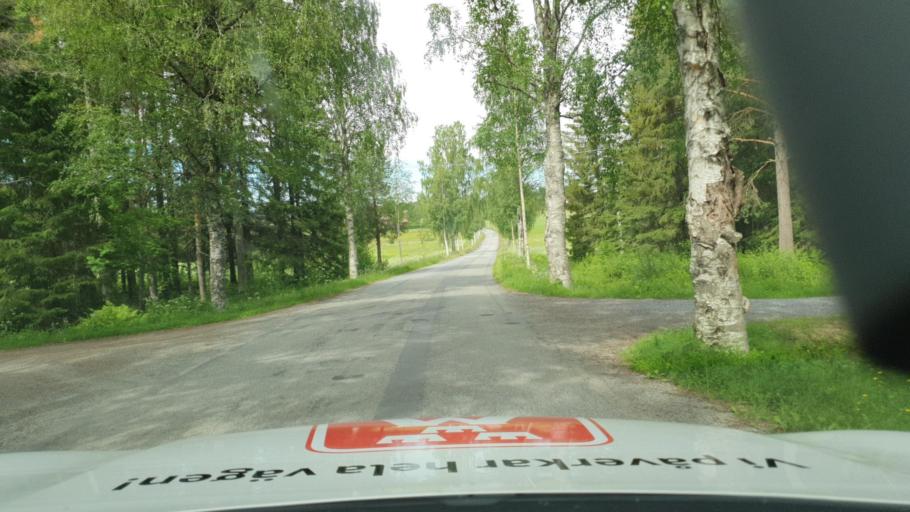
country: SE
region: Vaesterbotten
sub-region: Skelleftea Kommun
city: Burtraesk
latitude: 64.4457
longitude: 20.4837
